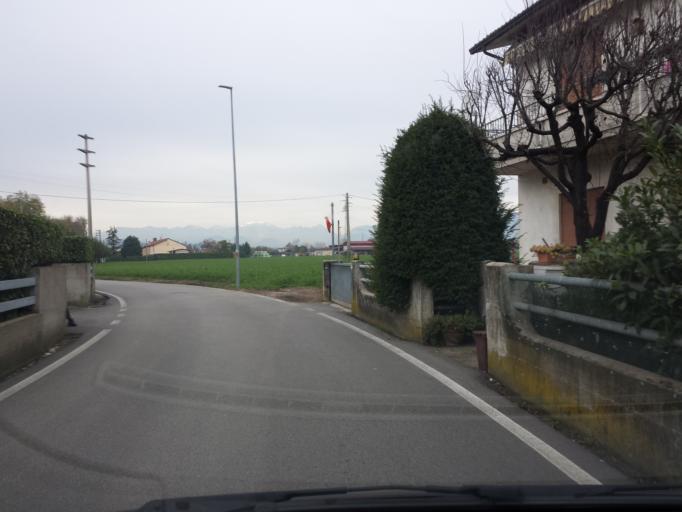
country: IT
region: Veneto
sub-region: Provincia di Vicenza
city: Sandrigo
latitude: 45.6674
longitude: 11.5960
